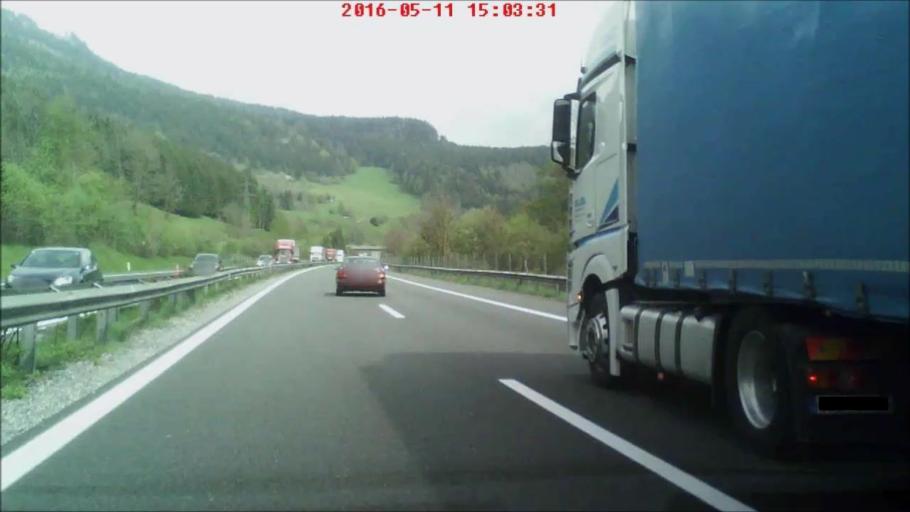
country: AT
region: Styria
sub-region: Politischer Bezirk Leoben
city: Wald am Schoberpass
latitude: 47.4687
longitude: 14.6352
